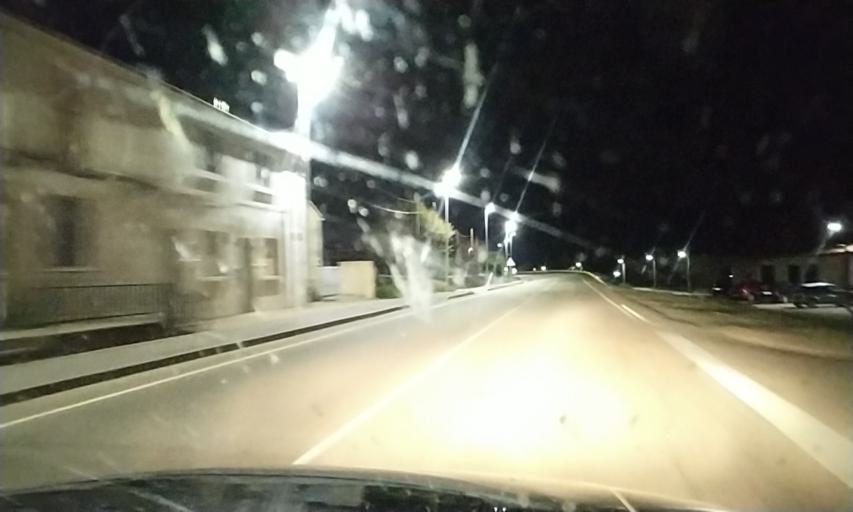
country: ES
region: Castille and Leon
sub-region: Provincia de Salamanca
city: Robleda
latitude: 40.3874
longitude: -6.6077
